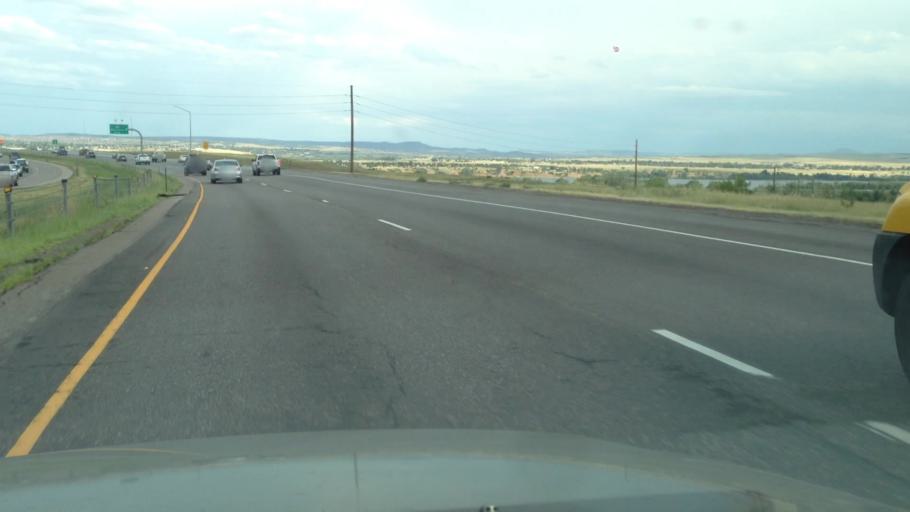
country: US
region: Colorado
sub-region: Jefferson County
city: Ken Caryl
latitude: 39.5547
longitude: -105.0939
